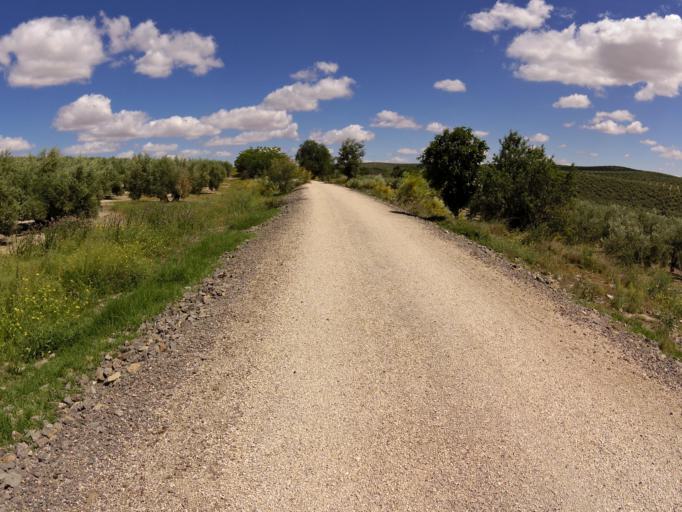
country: ES
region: Andalusia
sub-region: Provincia de Jaen
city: Alcaudete
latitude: 37.6519
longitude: -4.0617
